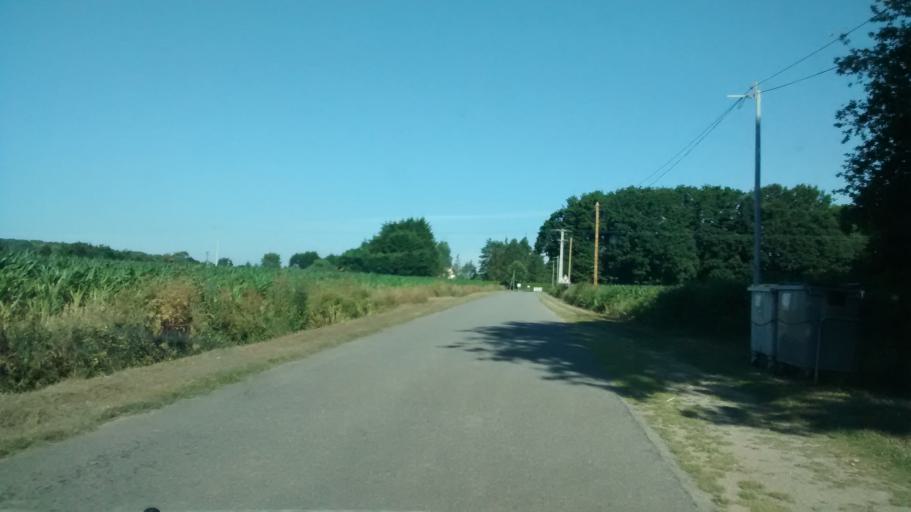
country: FR
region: Brittany
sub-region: Departement du Morbihan
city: Malestroit
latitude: 47.7876
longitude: -2.4312
